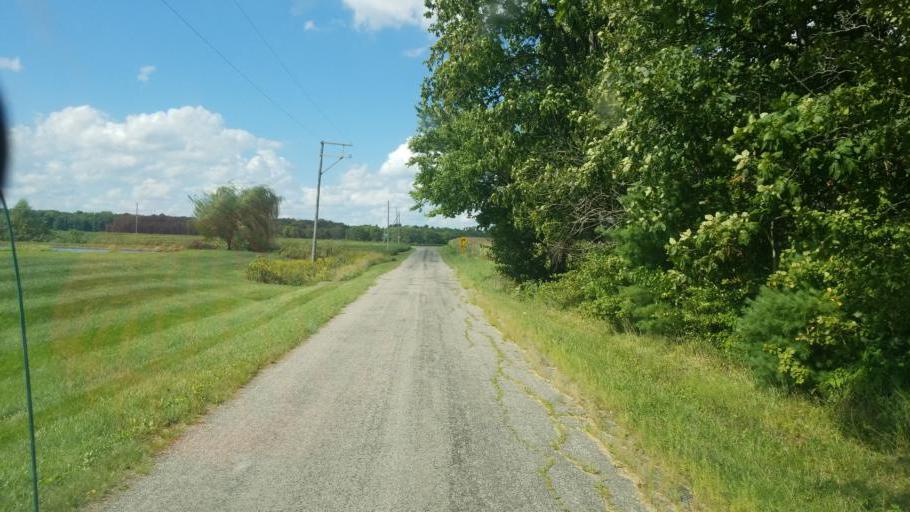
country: US
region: Ohio
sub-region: Union County
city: Richwood
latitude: 40.4649
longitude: -83.3434
